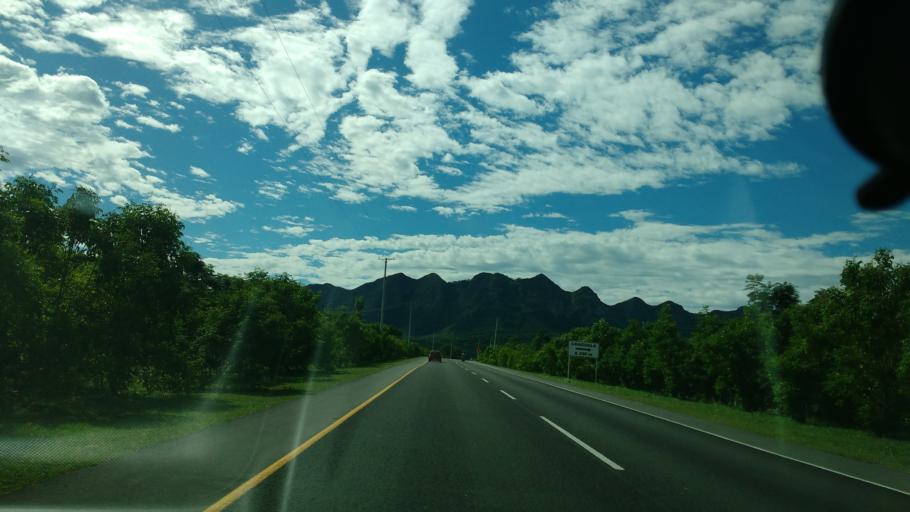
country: CO
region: Tolima
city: Valle de San Juan
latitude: 4.2661
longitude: -74.9982
